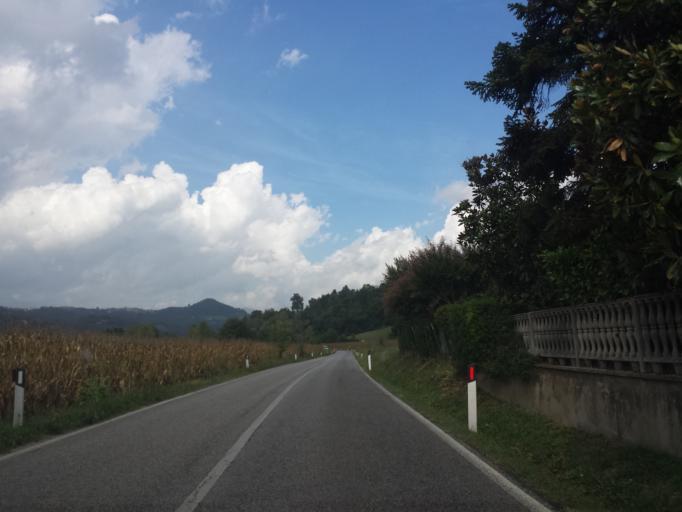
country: IT
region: Veneto
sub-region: Provincia di Vicenza
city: Sovizzo
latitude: 45.5424
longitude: 11.4351
